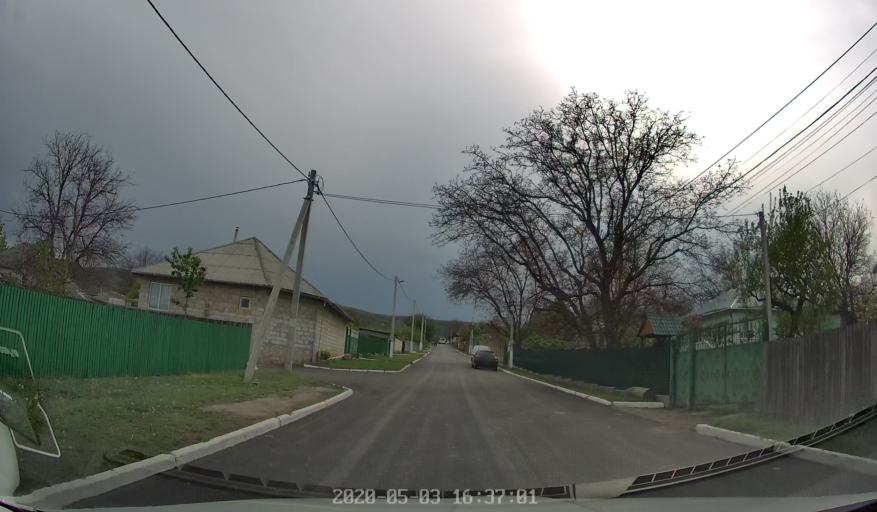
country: MD
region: Calarasi
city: Calarasi
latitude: 47.1931
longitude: 28.3584
